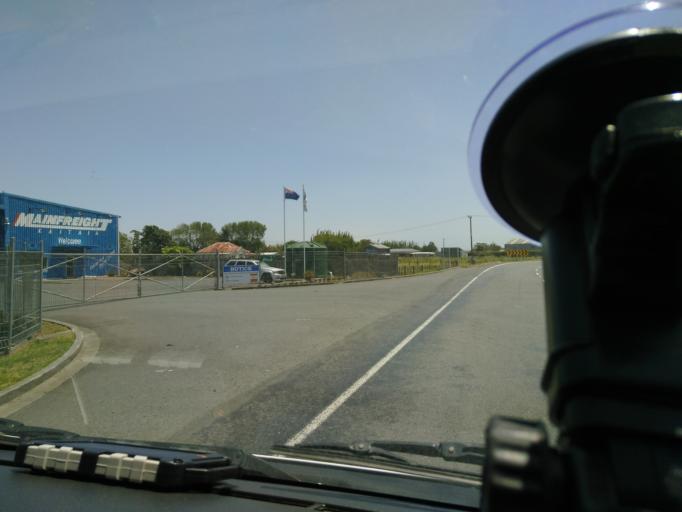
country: NZ
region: Northland
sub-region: Far North District
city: Kaitaia
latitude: -35.0914
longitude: 173.2568
